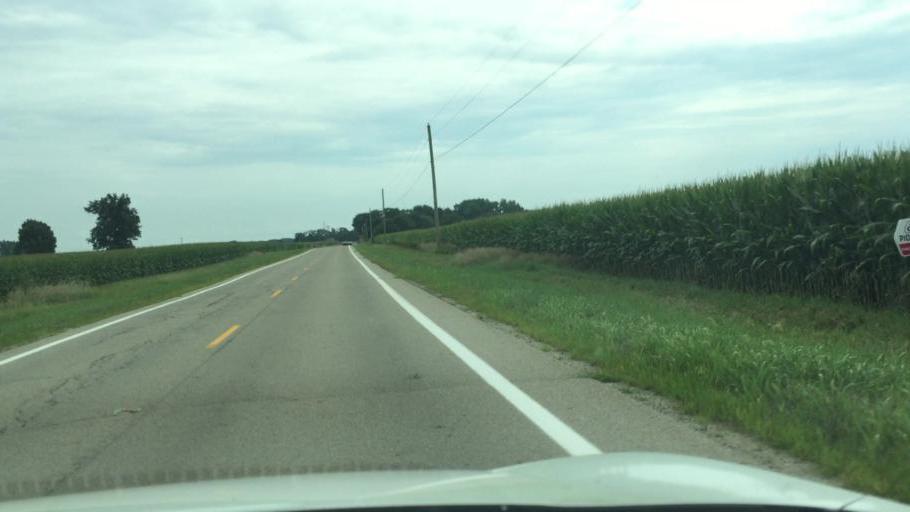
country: US
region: Ohio
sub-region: Champaign County
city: Mechanicsburg
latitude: 40.1472
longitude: -83.5292
